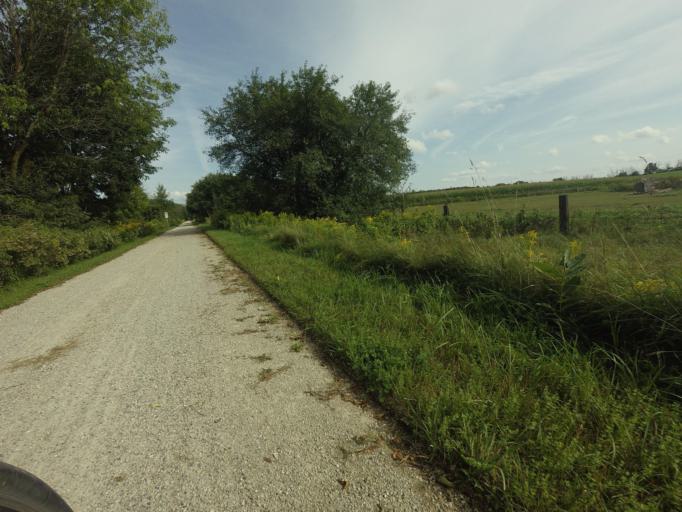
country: CA
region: Ontario
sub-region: Wellington County
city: Guelph
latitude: 43.5793
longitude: -80.3892
